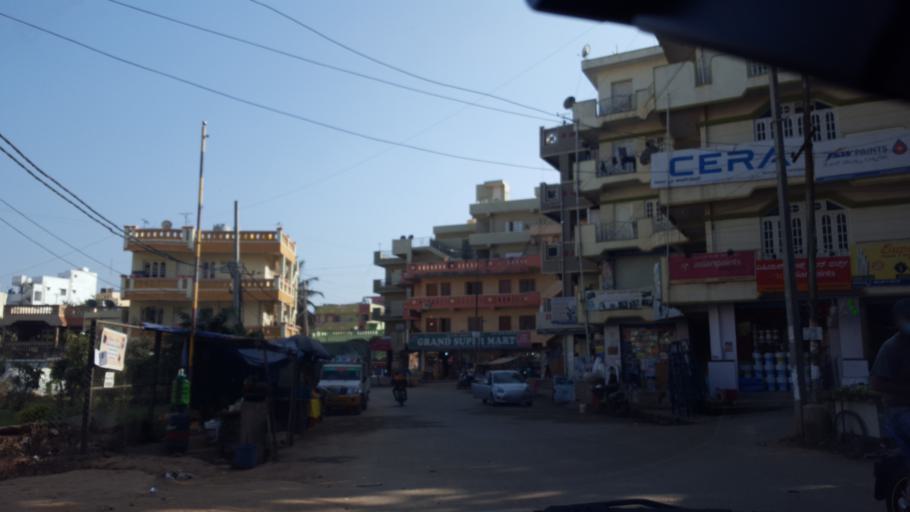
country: IN
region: Karnataka
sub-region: Bangalore Urban
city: Bangalore
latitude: 12.9506
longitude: 77.7069
